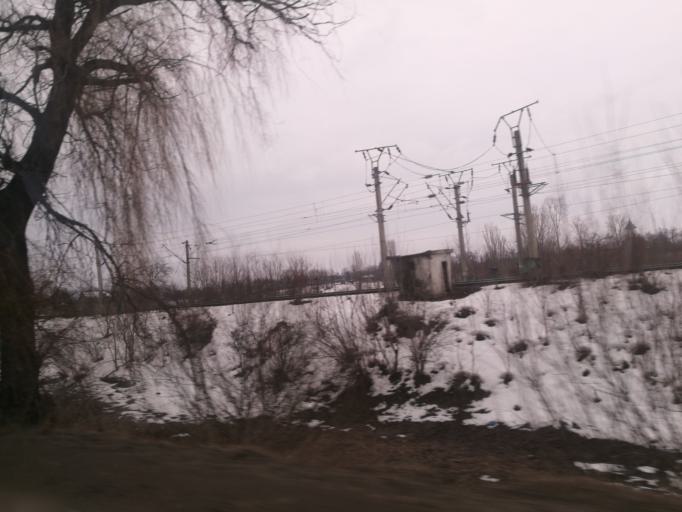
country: RO
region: Iasi
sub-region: Comuna Ruginoasa
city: Ruginoasa
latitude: 47.2435
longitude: 26.8505
